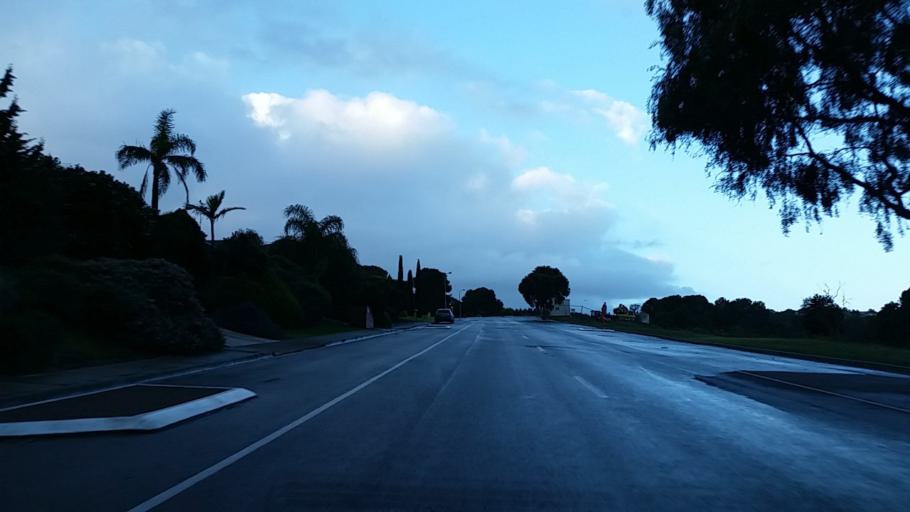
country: AU
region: South Australia
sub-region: Marion
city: Marino
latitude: -35.0714
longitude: 138.5075
